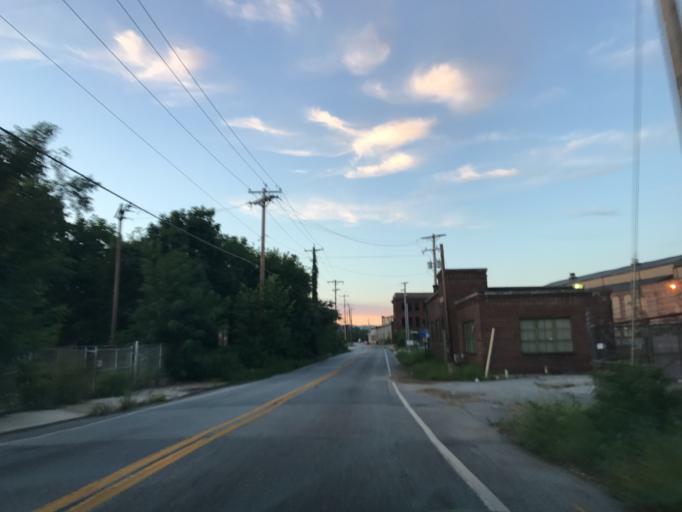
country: US
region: Pennsylvania
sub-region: York County
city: York
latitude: 39.9707
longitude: -76.7248
